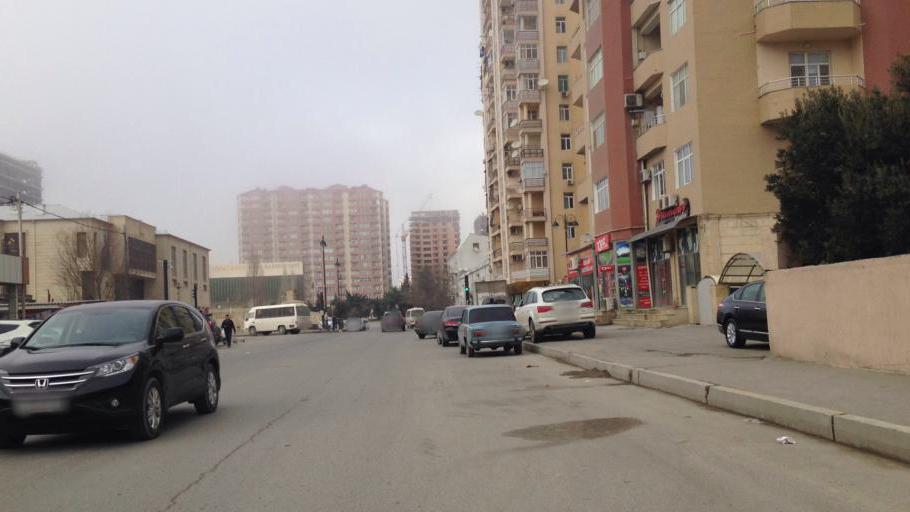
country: AZ
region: Baki
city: Baku
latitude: 40.3813
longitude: 49.8759
